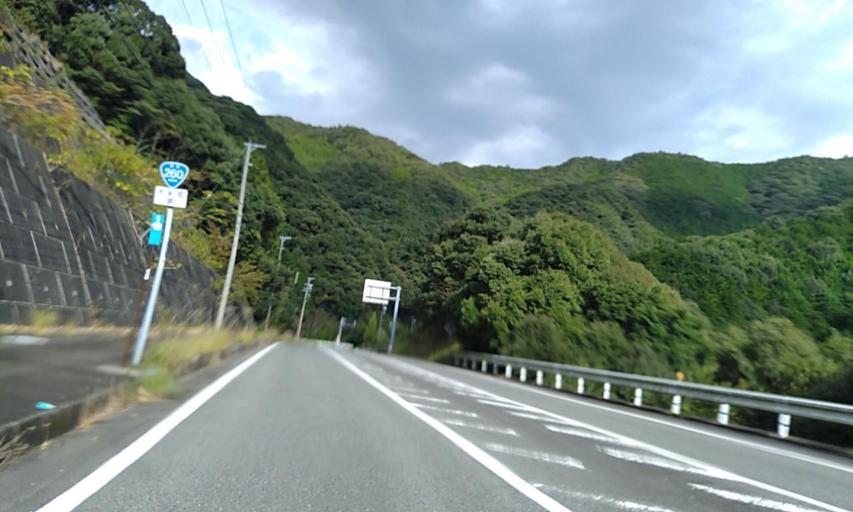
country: JP
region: Mie
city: Owase
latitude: 34.2502
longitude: 136.4043
